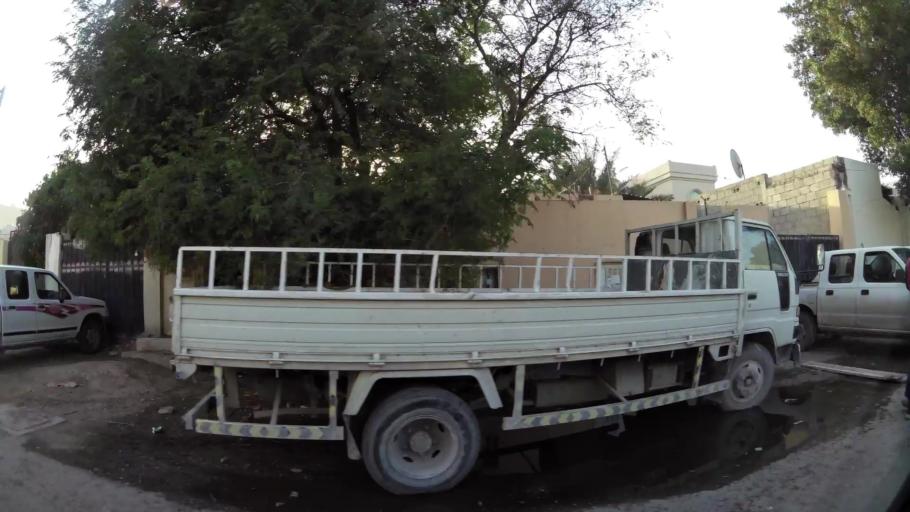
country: QA
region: Baladiyat ar Rayyan
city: Ar Rayyan
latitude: 25.3260
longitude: 51.4583
